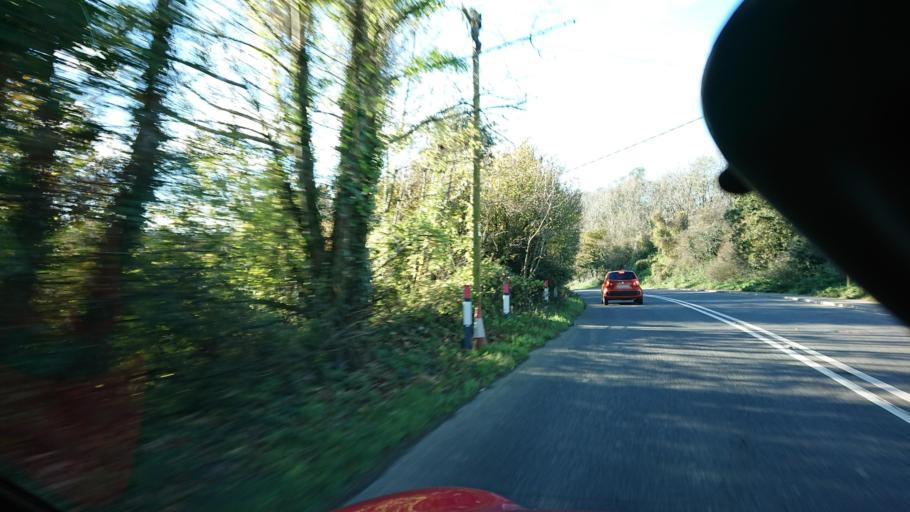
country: GB
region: England
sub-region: Cornwall
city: Pillaton
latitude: 50.4161
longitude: -4.3193
